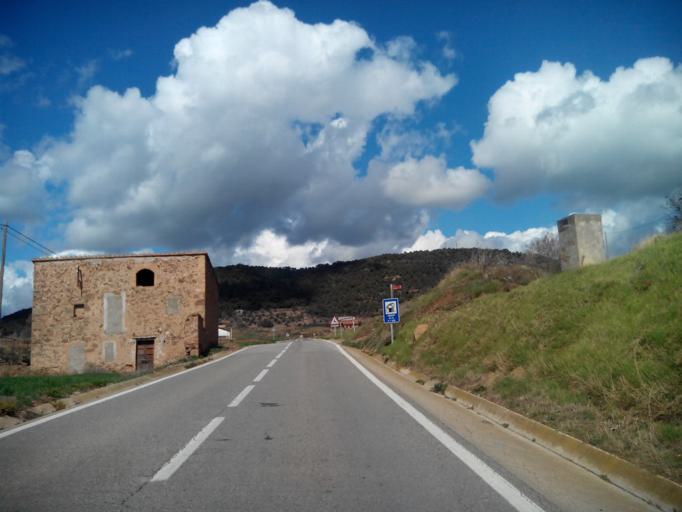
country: ES
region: Catalonia
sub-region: Provincia de Barcelona
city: Cardona
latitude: 41.9233
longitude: 1.6823
